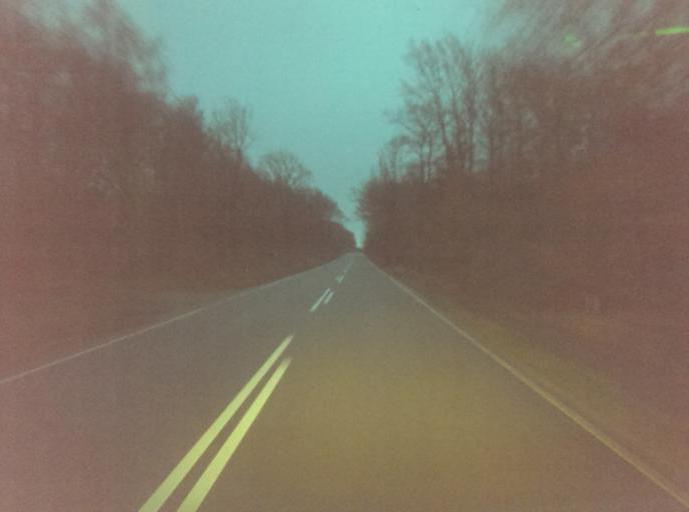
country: DK
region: South Denmark
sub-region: Esbjerg Kommune
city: Tjaereborg
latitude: 55.4883
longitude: 8.5789
